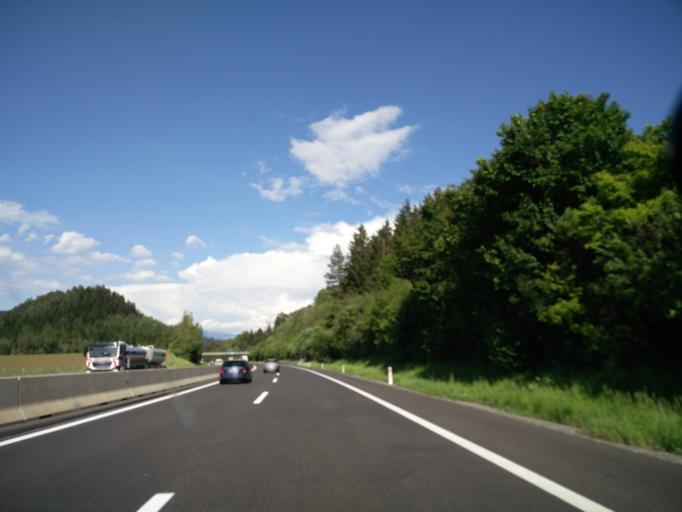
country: AT
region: Carinthia
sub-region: Politischer Bezirk Volkermarkt
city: Voelkermarkt
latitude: 46.6788
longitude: 14.6316
